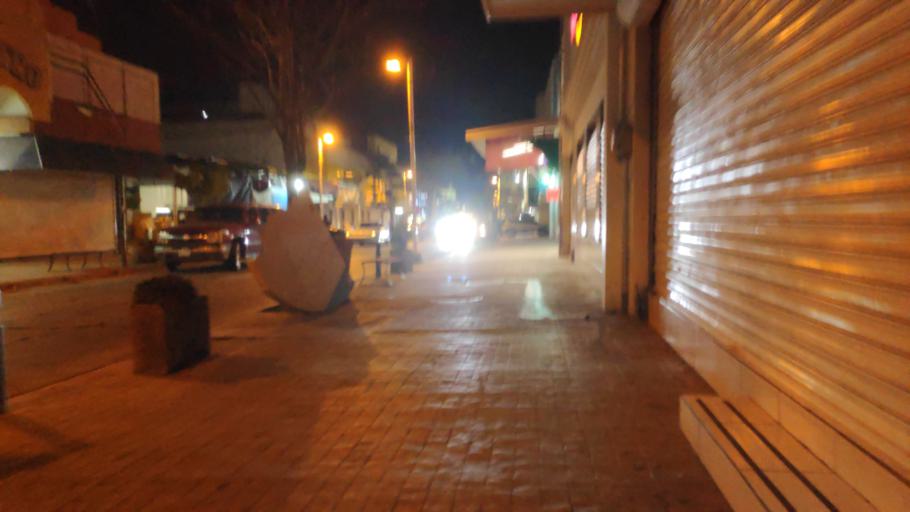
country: MX
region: Sinaloa
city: Culiacan
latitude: 24.8085
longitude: -107.3979
